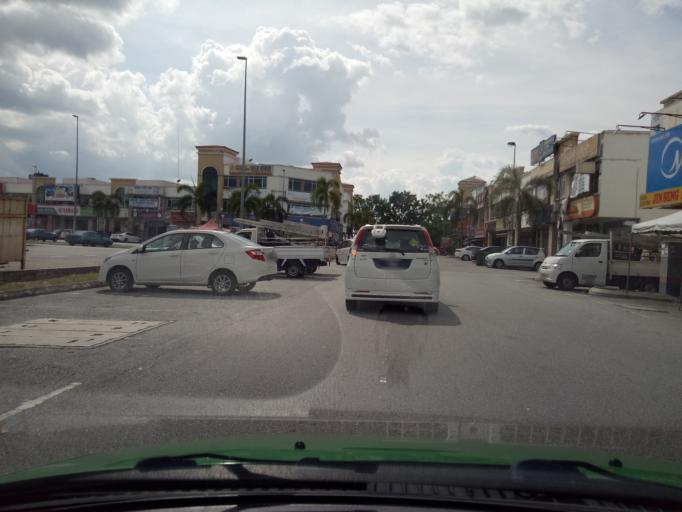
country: MY
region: Selangor
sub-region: Hulu Langat
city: Semenyih
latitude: 2.9314
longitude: 101.8575
